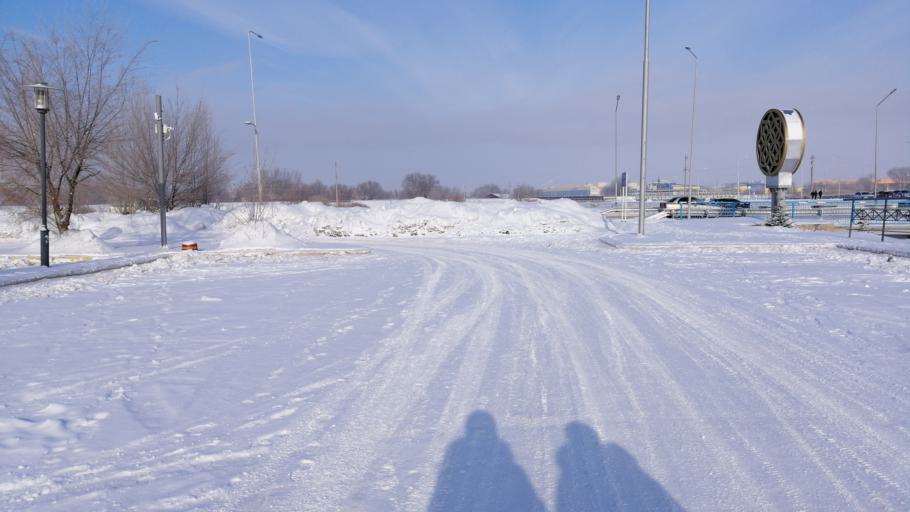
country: KZ
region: Aqtoebe
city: Aqtobe
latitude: 50.2898
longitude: 57.1946
